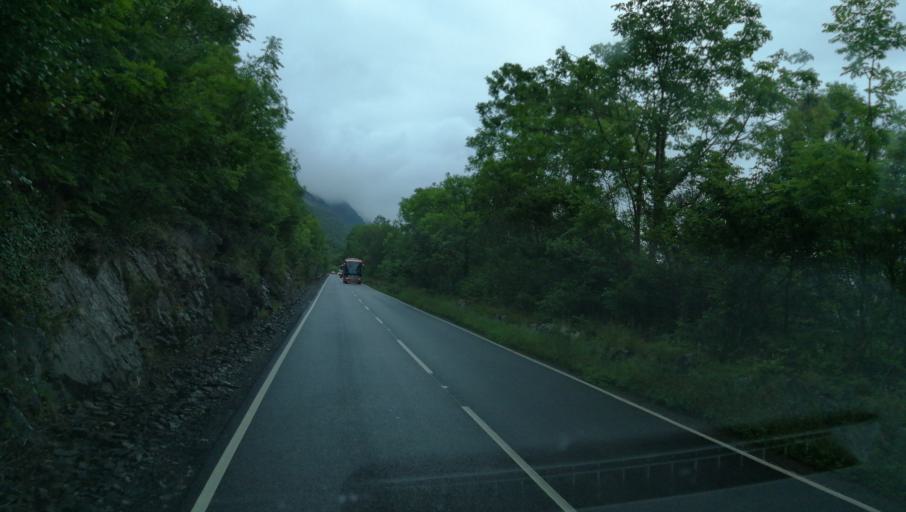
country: GB
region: Scotland
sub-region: Highland
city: Beauly
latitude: 57.3714
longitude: -4.3860
